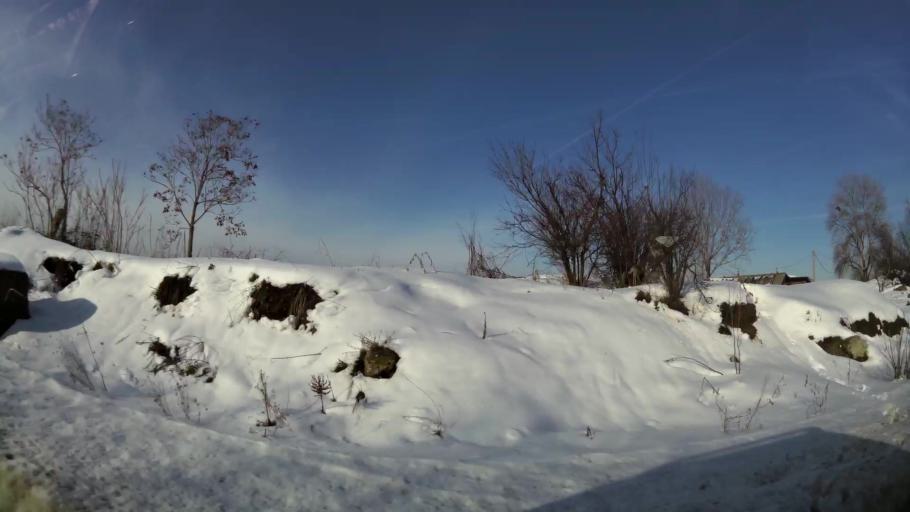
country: RS
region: Central Serbia
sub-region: Belgrade
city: Palilula
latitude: 44.8220
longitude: 20.4933
